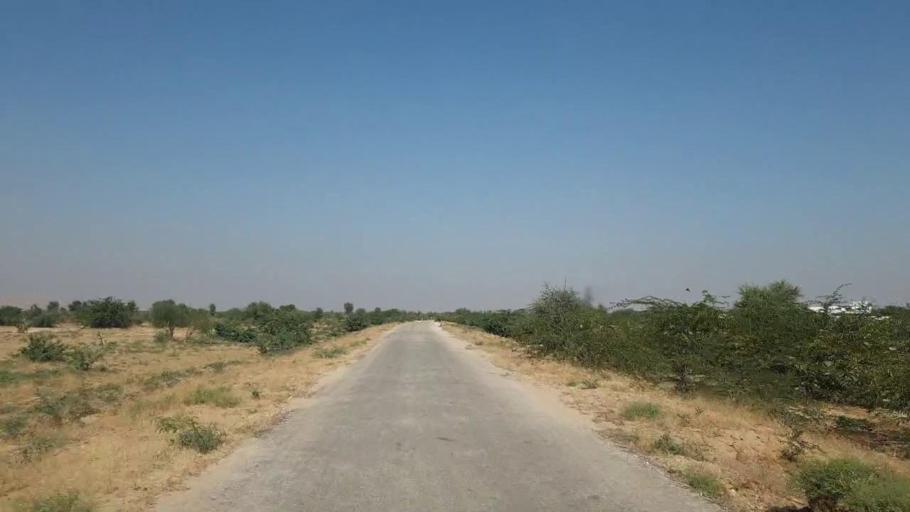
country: PK
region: Sindh
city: Jamshoro
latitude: 25.3747
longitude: 67.8419
